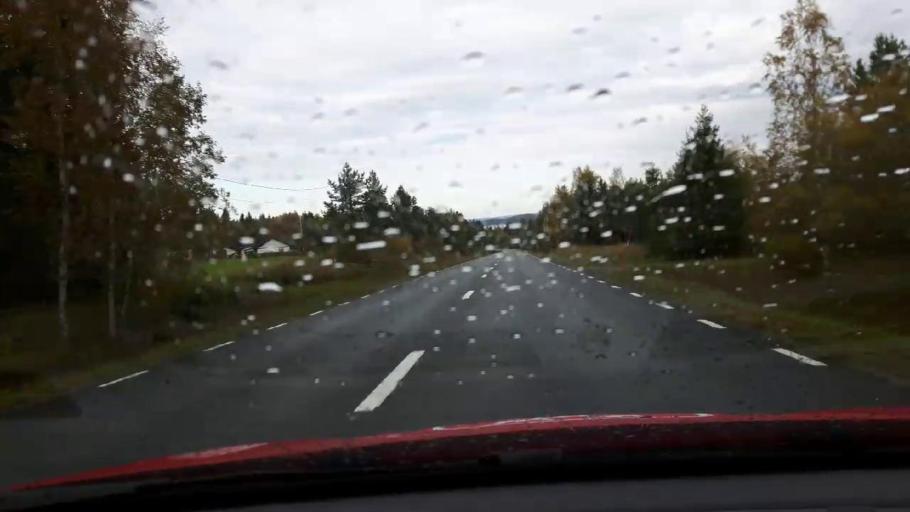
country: SE
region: Jaemtland
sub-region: Krokoms Kommun
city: Krokom
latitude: 63.1186
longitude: 14.2935
